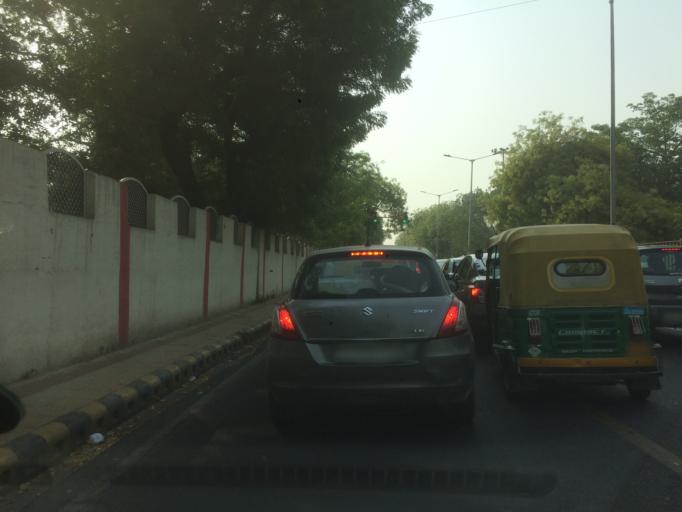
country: IN
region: NCT
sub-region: Central Delhi
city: Karol Bagh
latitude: 28.5980
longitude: 77.1455
